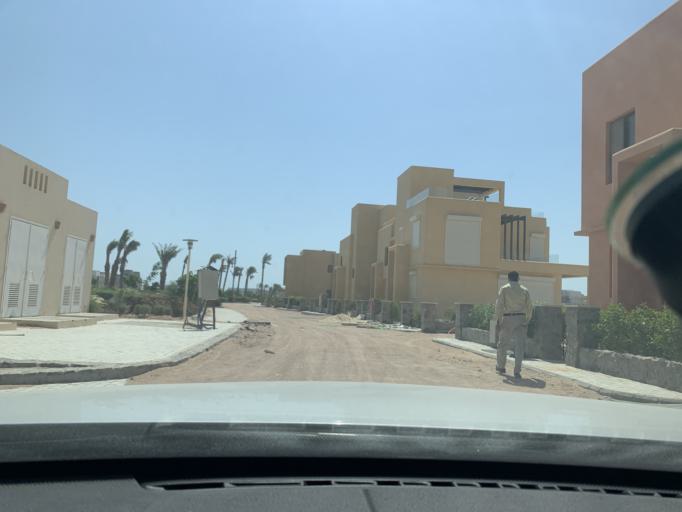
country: EG
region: Red Sea
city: El Gouna
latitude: 27.4037
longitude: 33.6599
